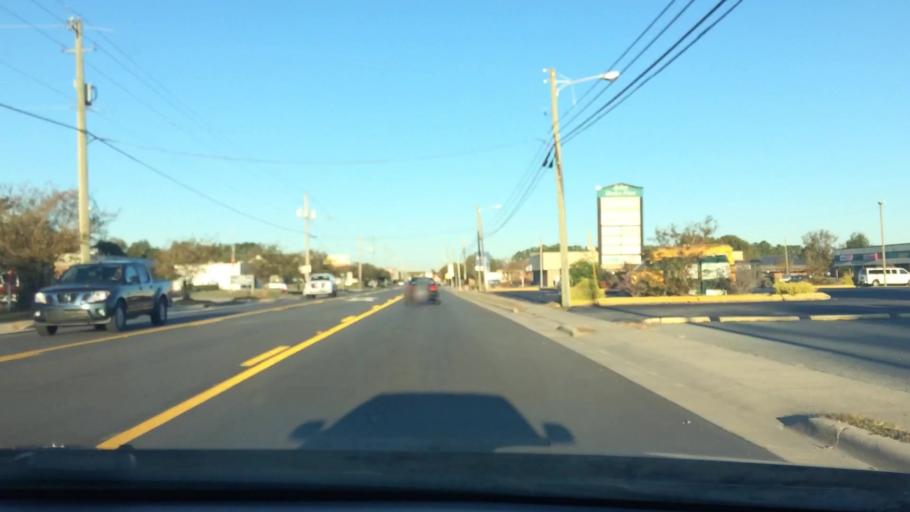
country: US
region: North Carolina
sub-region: Pitt County
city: Ayden
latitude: 35.4735
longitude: -77.4285
